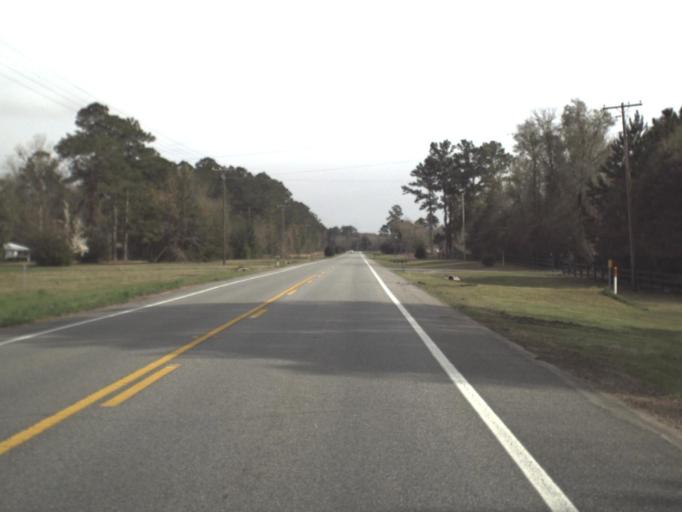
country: US
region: Florida
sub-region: Jefferson County
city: Monticello
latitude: 30.5138
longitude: -83.7785
